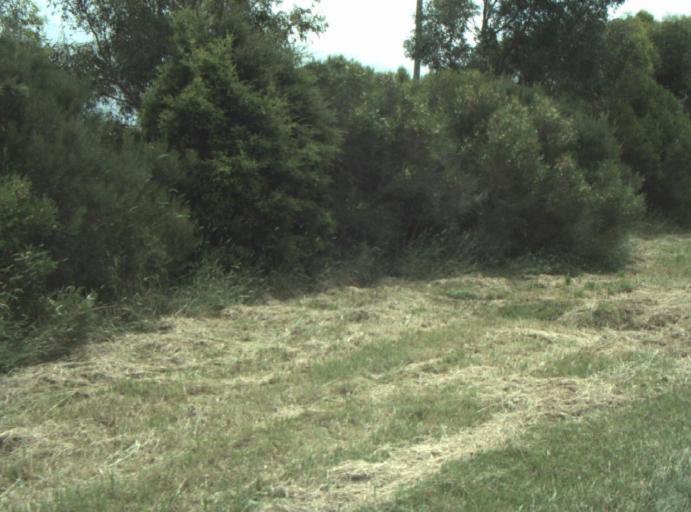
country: AU
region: Victoria
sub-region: Greater Geelong
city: Wandana Heights
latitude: -38.2392
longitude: 144.2969
